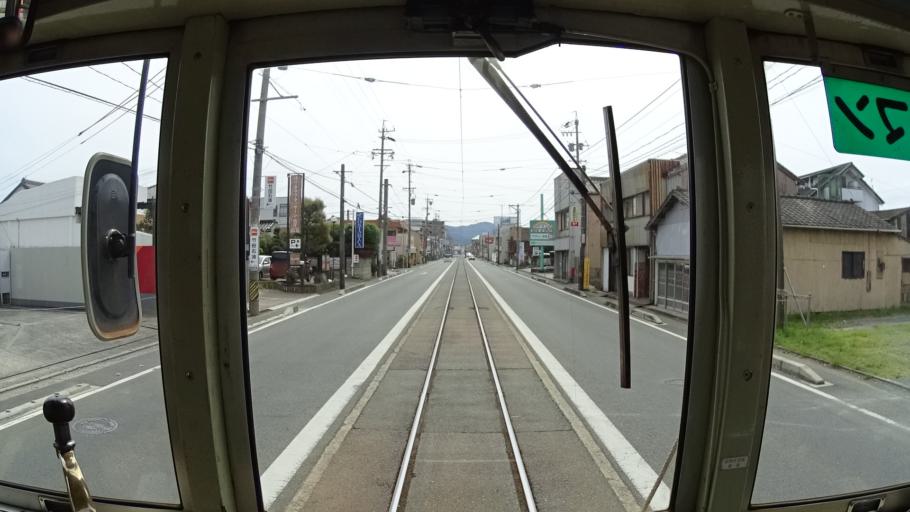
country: JP
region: Aichi
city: Toyohashi
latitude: 34.7647
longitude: 137.4195
